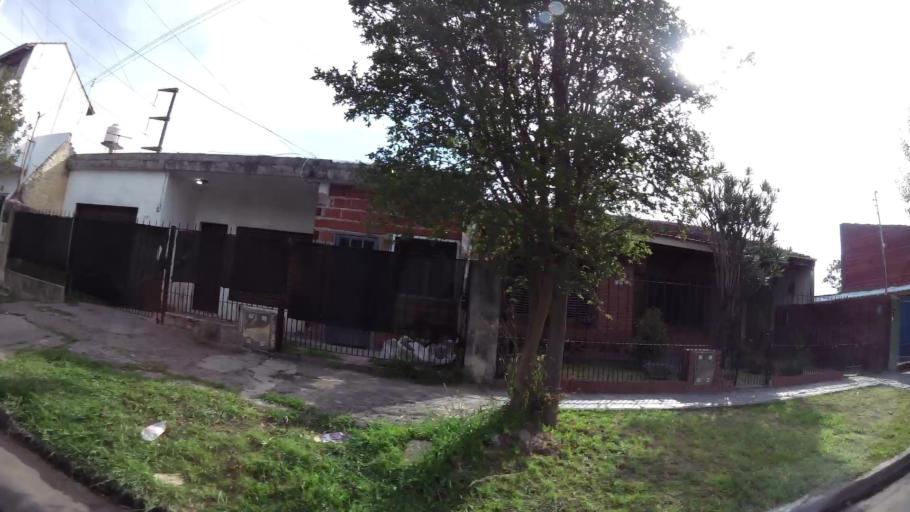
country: AR
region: Buenos Aires
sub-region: Partido de Quilmes
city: Quilmes
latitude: -34.7575
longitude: -58.2716
